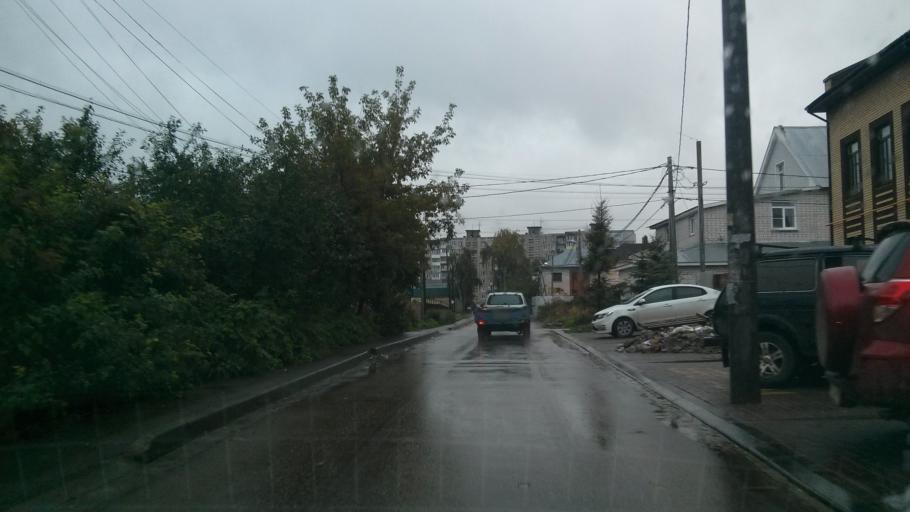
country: RU
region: Nizjnij Novgorod
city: Nizhniy Novgorod
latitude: 56.3059
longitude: 44.0349
